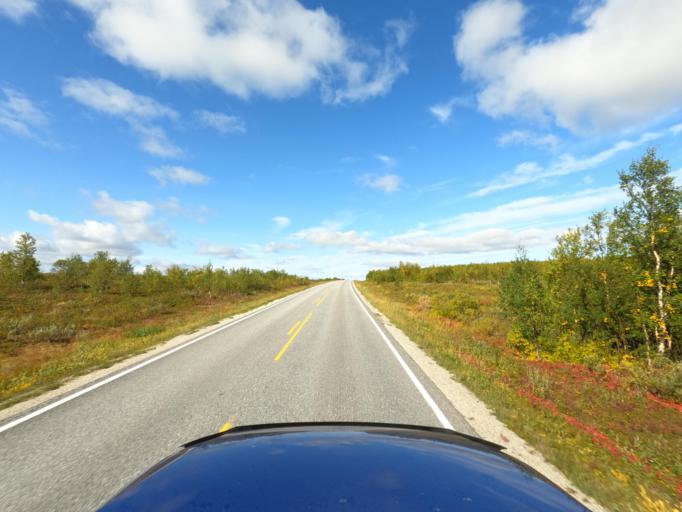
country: NO
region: Finnmark Fylke
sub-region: Karasjok
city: Karasjohka
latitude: 69.5535
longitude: 25.4057
